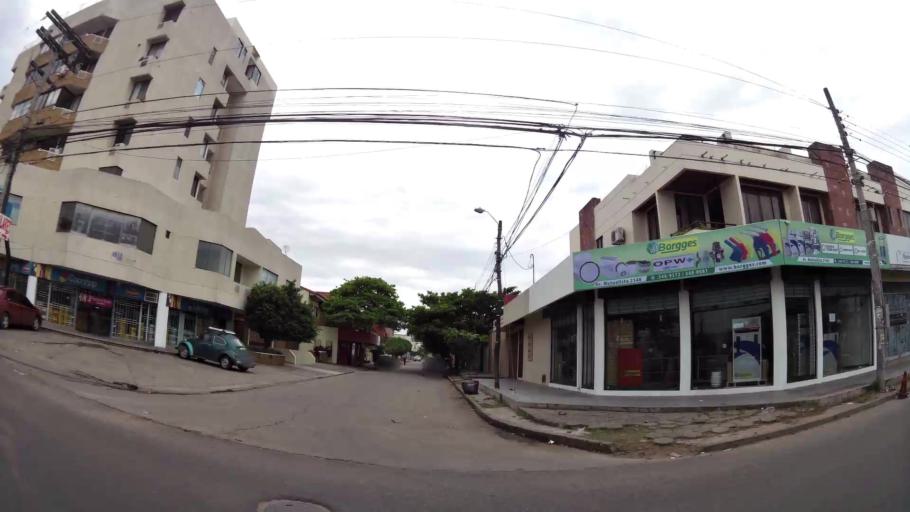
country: BO
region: Santa Cruz
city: Santa Cruz de la Sierra
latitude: -17.7697
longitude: -63.1659
